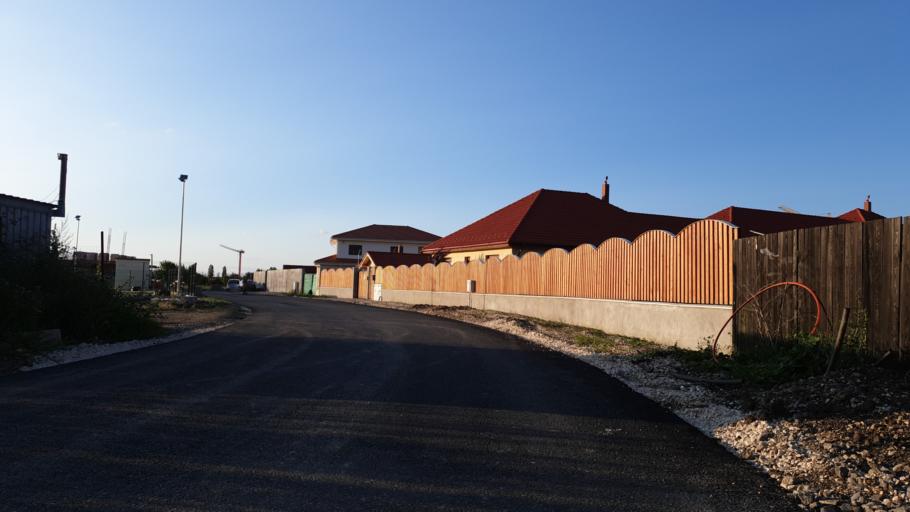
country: RO
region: Brasov
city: Brasov
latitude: 45.6757
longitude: 25.6050
